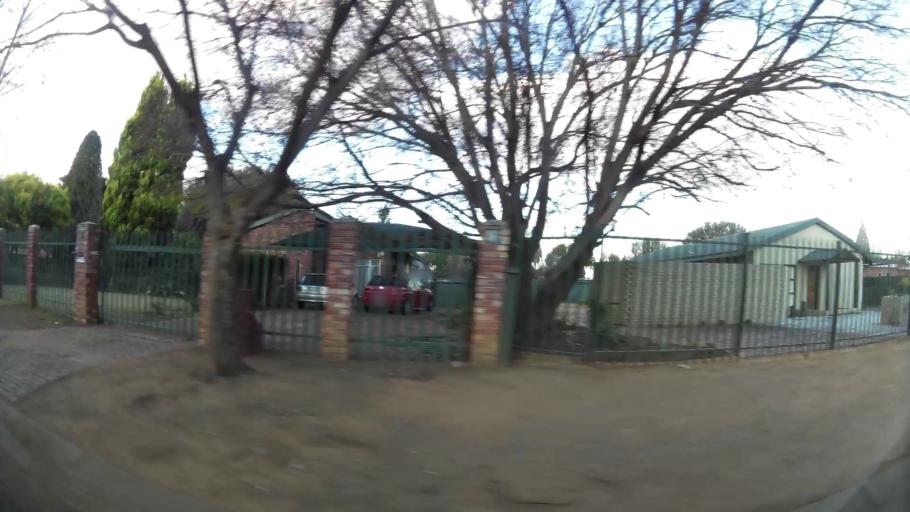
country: ZA
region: North-West
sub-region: Dr Kenneth Kaunda District Municipality
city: Potchefstroom
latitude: -26.7399
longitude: 27.0933
